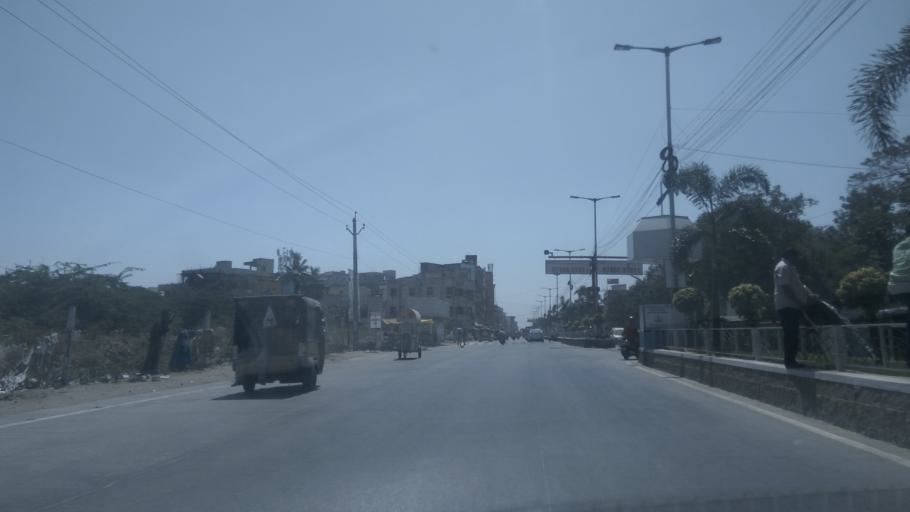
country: IN
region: Andhra Pradesh
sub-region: Chittoor
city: Tirupati
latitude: 13.6196
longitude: 79.4324
